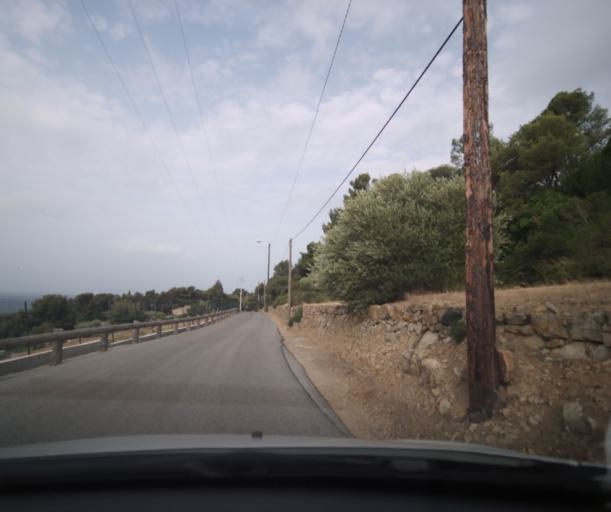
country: FR
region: Provence-Alpes-Cote d'Azur
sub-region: Departement du Var
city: Carqueiranne
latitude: 43.0814
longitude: 6.0474
